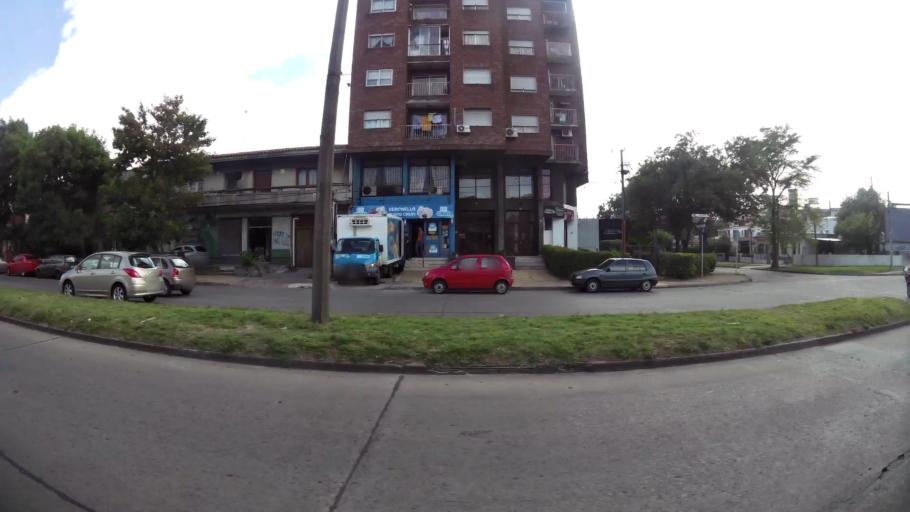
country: UY
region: Montevideo
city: Montevideo
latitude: -34.8748
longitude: -56.1540
